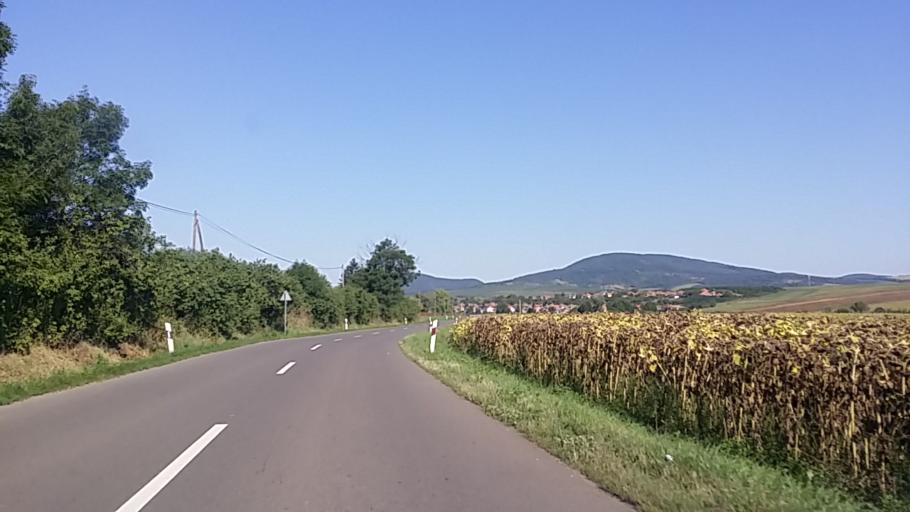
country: HU
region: Nograd
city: Bujak
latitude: 47.8871
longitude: 19.6169
